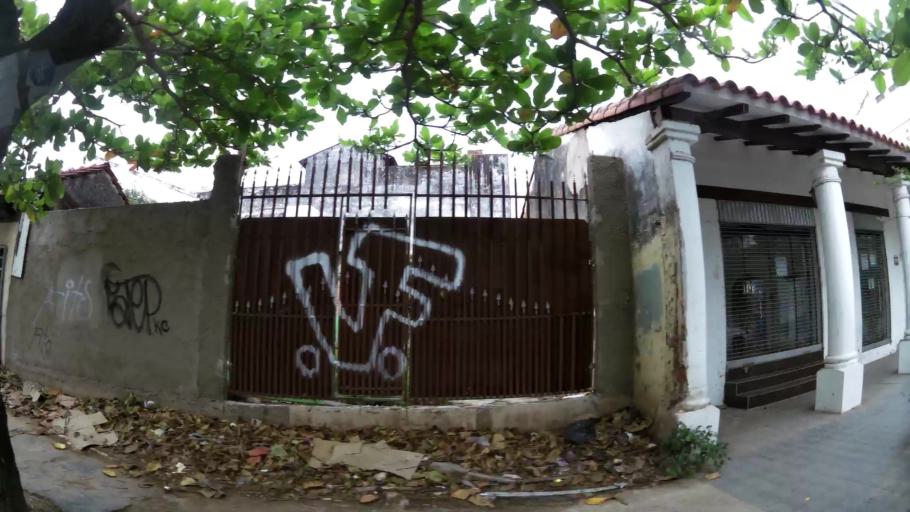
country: BO
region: Santa Cruz
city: Santa Cruz de la Sierra
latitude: -17.7836
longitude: -63.1761
